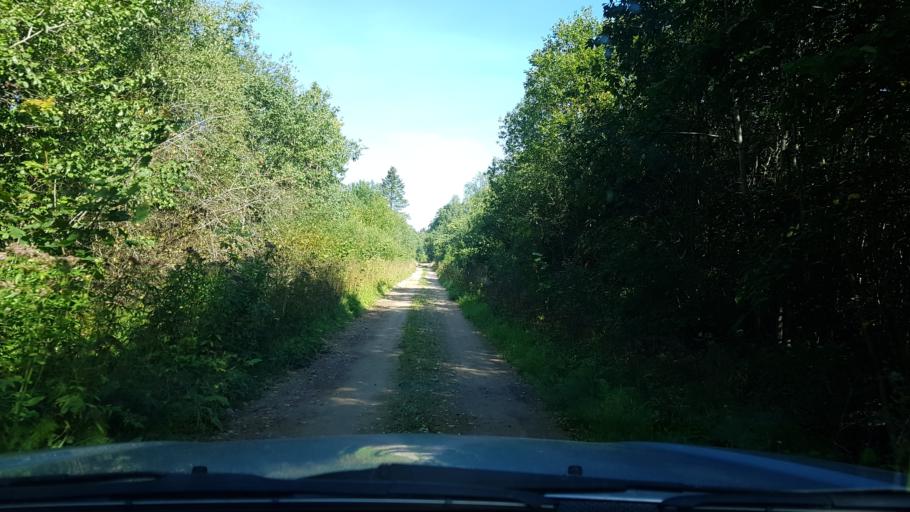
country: EE
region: Ida-Virumaa
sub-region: Sillamaee linn
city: Sillamae
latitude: 59.3429
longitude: 27.7354
